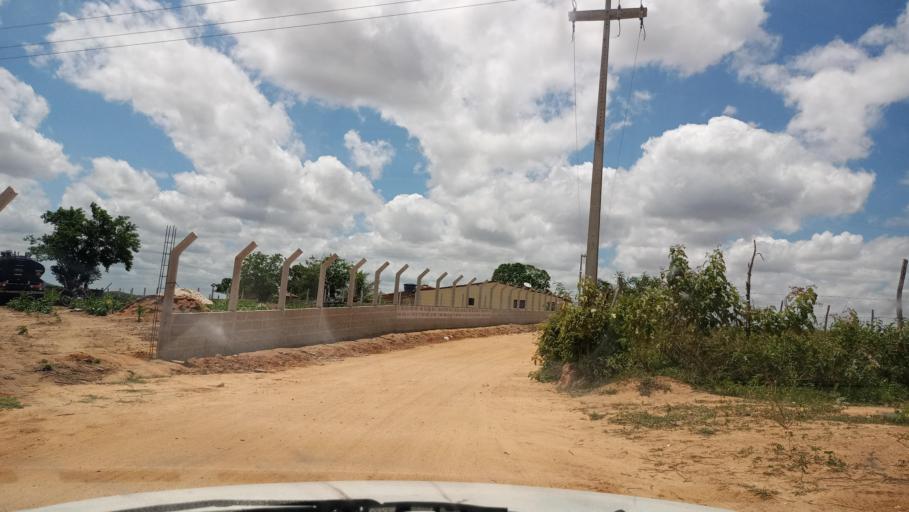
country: BR
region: Rio Grande do Norte
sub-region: Sao Jose Do Campestre
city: Sao Jose do Campestre
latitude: -6.4384
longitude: -35.6324
